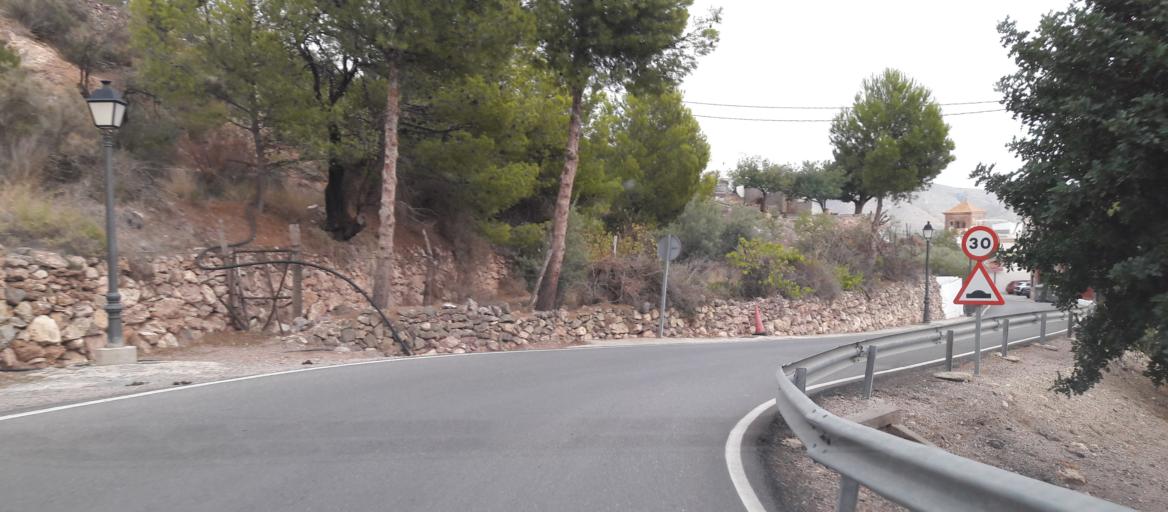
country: ES
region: Andalusia
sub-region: Provincia de Almeria
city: Enix
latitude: 36.8776
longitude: -2.6039
